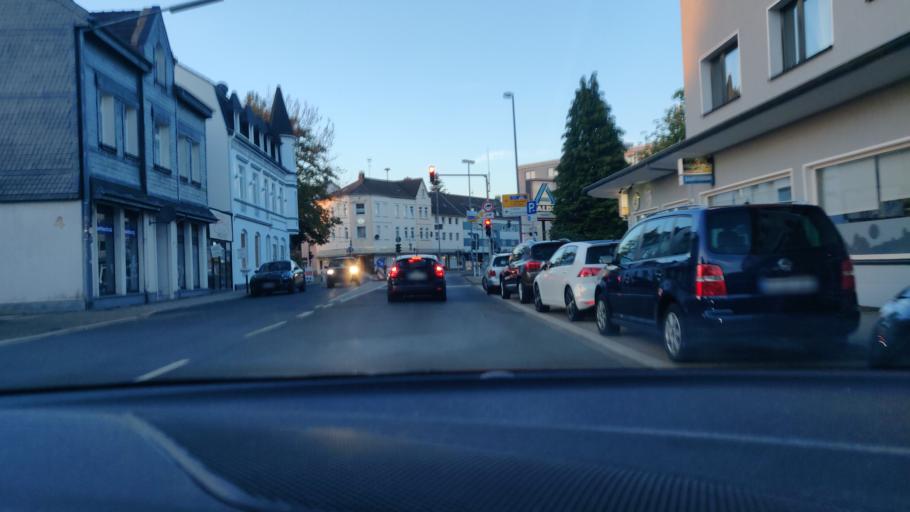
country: DE
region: North Rhine-Westphalia
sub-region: Regierungsbezirk Dusseldorf
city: Velbert
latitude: 51.3126
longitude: 7.0667
